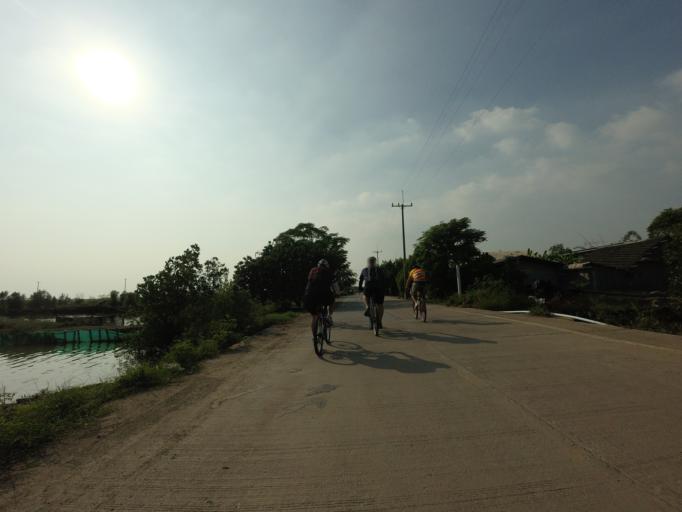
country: TH
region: Samut Sakhon
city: Samut Sakhon
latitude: 13.4982
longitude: 100.3459
